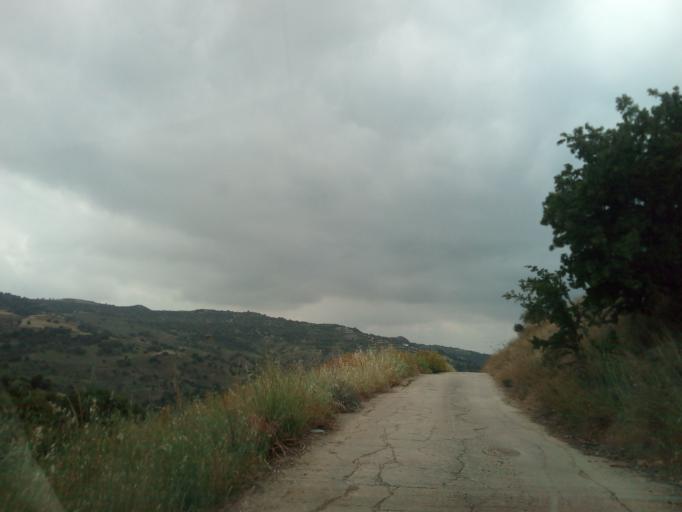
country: CY
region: Limassol
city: Pissouri
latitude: 34.8157
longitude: 32.6363
